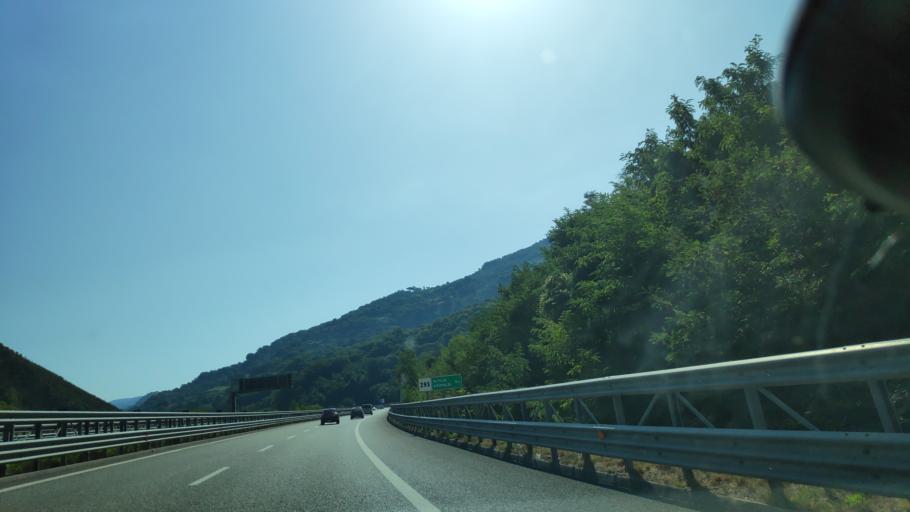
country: IT
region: Calabria
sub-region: Provincia di Catanzaro
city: San Mango d'Aquino
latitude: 39.0808
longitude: 16.2012
